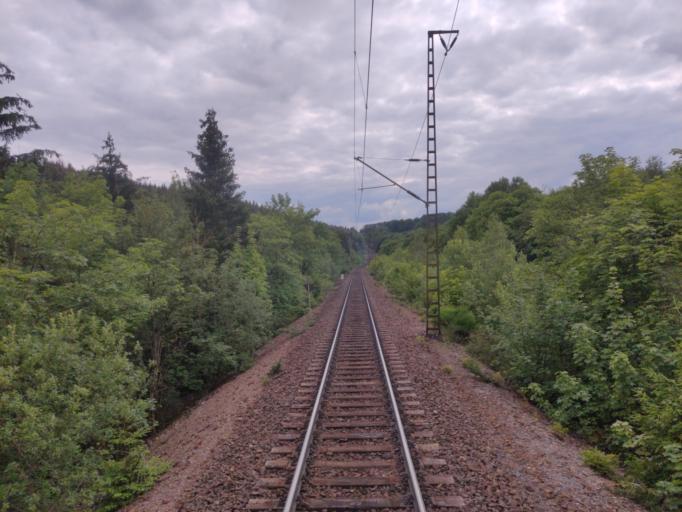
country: DE
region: Saxony-Anhalt
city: Huttenrode
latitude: 51.7815
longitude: 10.9130
